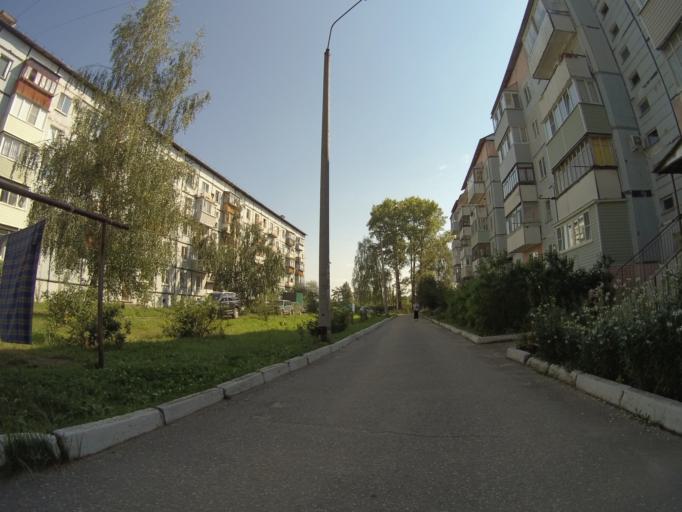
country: RU
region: Vladimir
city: Bogolyubovo
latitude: 56.2514
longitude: 40.5515
